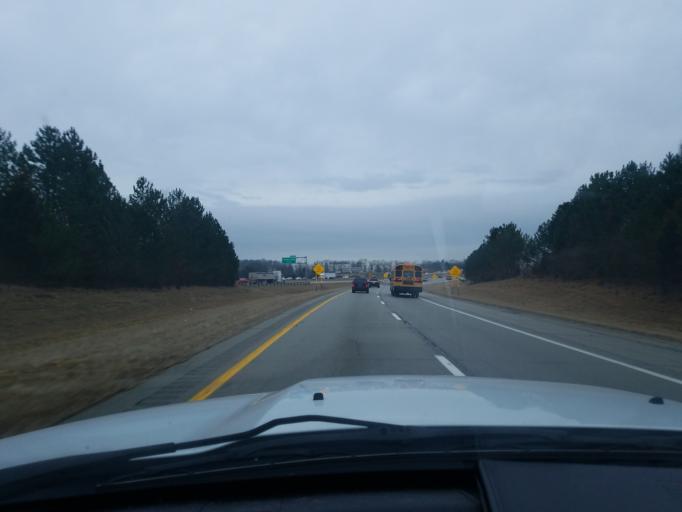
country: US
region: Ohio
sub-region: Montgomery County
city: West Carrollton City
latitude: 39.6166
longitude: -84.2336
